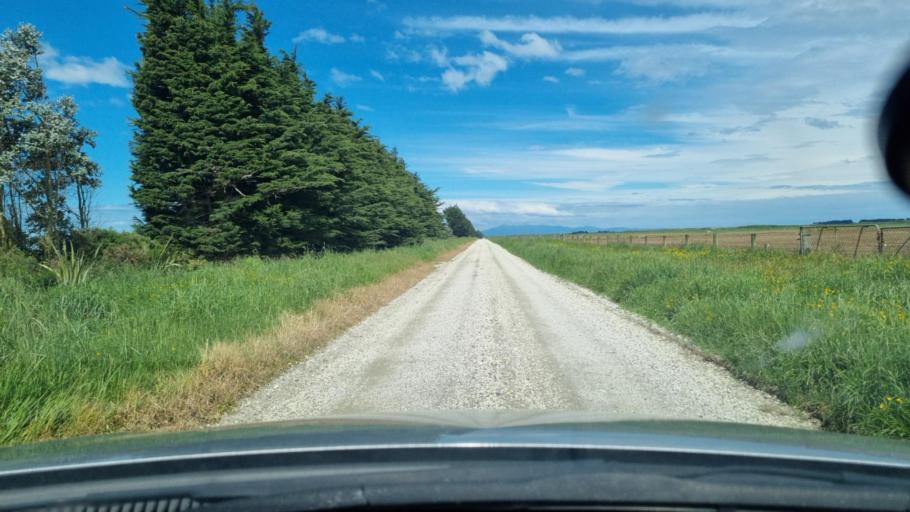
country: NZ
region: Southland
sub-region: Invercargill City
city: Invercargill
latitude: -46.3711
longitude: 168.2782
